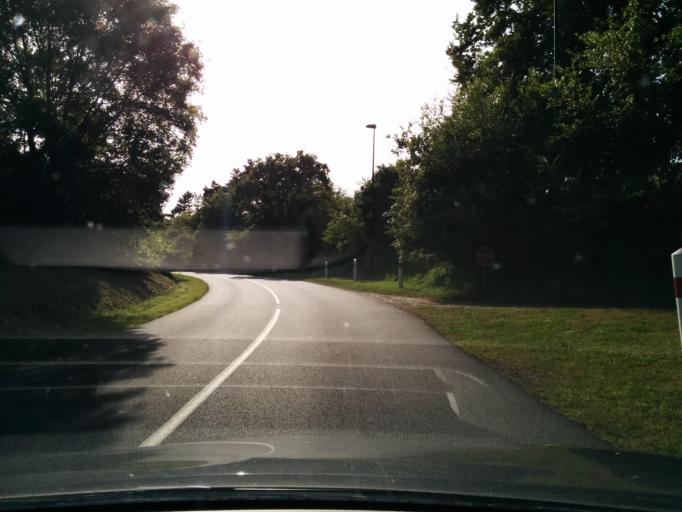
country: FR
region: Haute-Normandie
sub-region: Departement de l'Eure
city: Saint-Just
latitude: 49.1304
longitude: 1.4525
